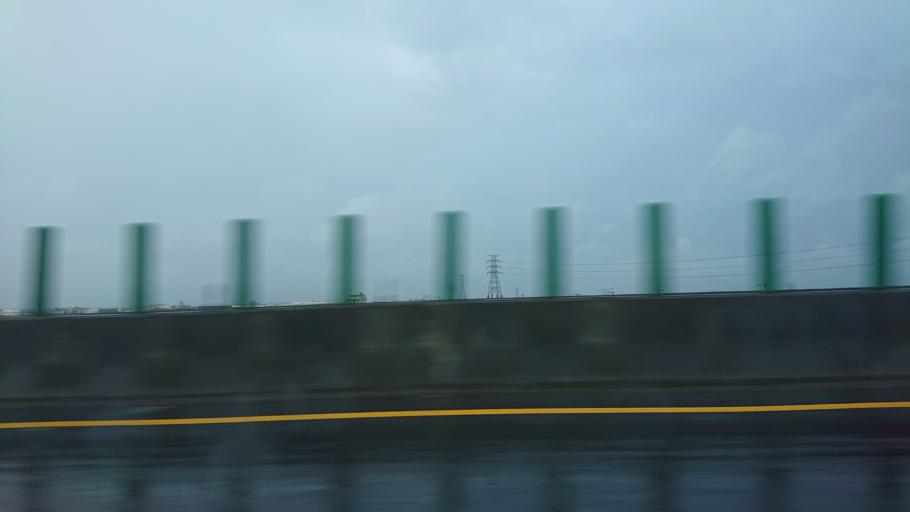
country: TW
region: Taiwan
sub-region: Changhua
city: Chang-hua
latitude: 24.1268
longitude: 120.4390
